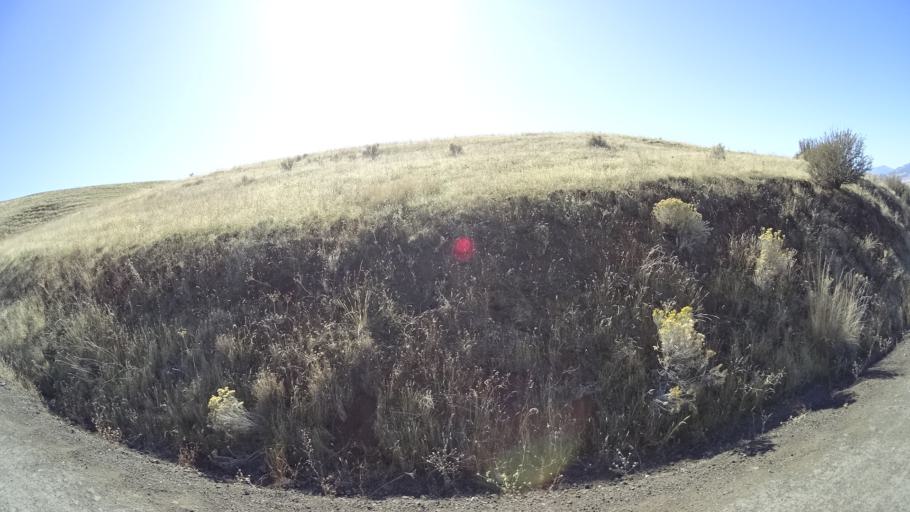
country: US
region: California
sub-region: Siskiyou County
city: Montague
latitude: 41.8158
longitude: -122.3697
